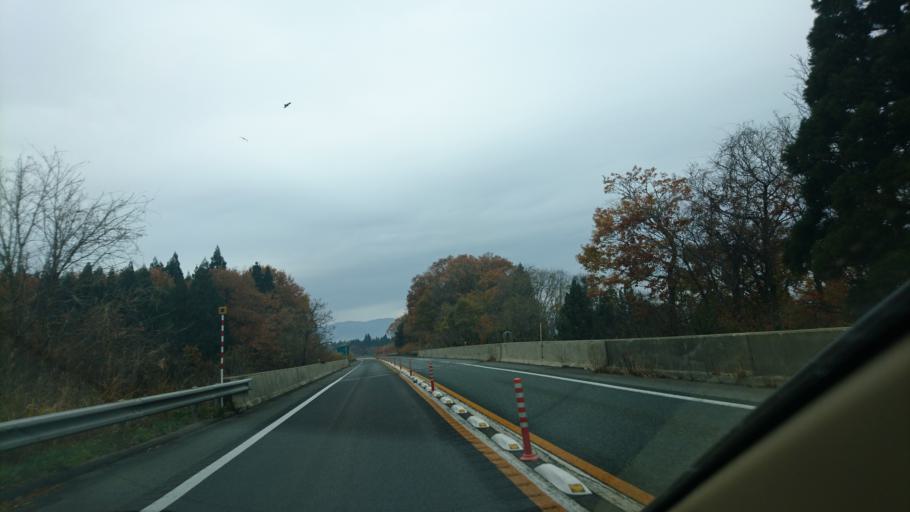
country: JP
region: Iwate
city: Kitakami
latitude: 39.2869
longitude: 140.9937
